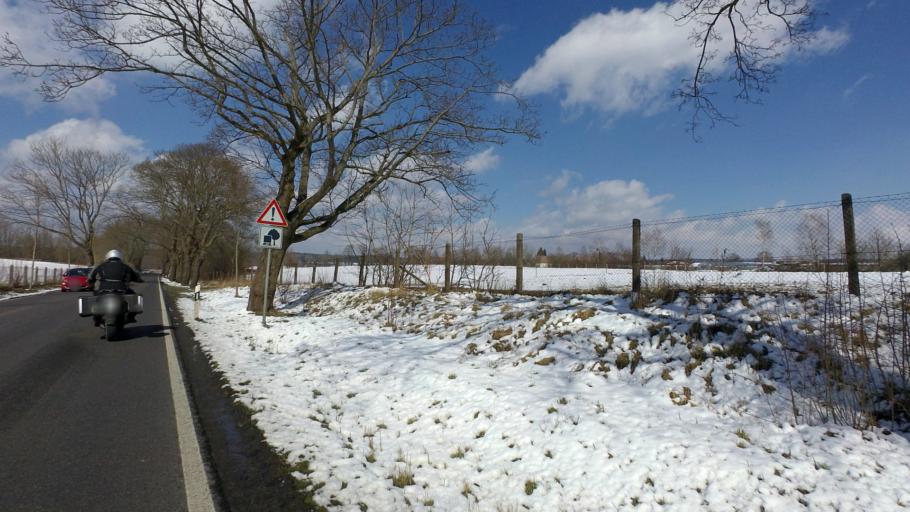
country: DE
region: Brandenburg
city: Britz
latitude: 52.8818
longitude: 13.7284
